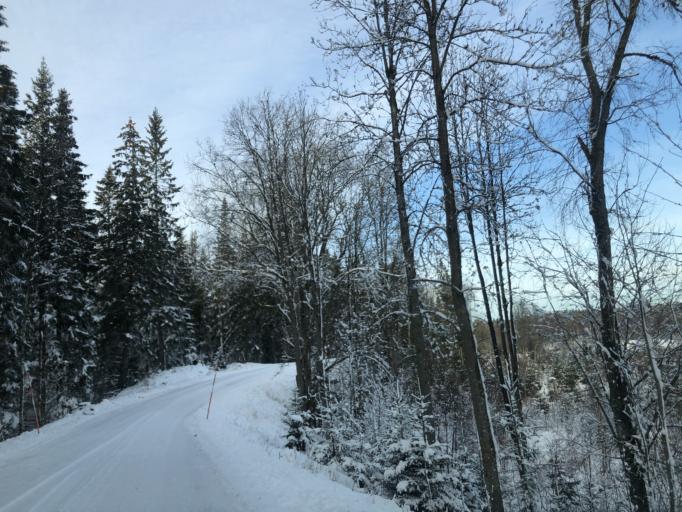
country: SE
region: Vaestra Goetaland
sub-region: Ulricehamns Kommun
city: Ulricehamn
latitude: 57.7670
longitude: 13.5203
